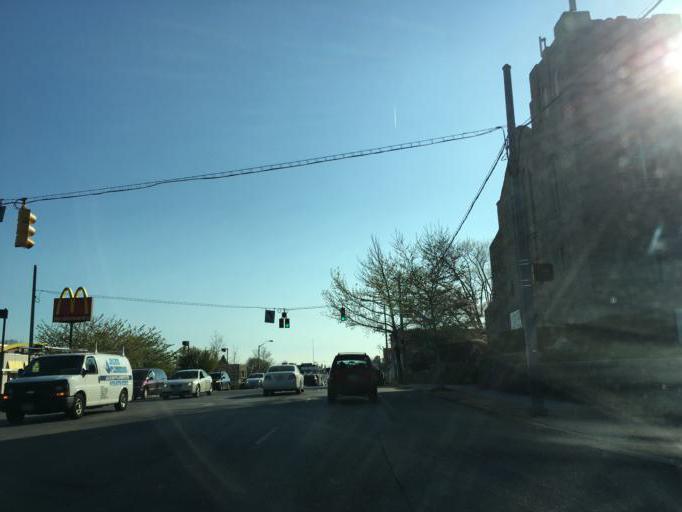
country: US
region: Maryland
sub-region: Baltimore County
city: Overlea
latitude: 39.3437
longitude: -76.5437
